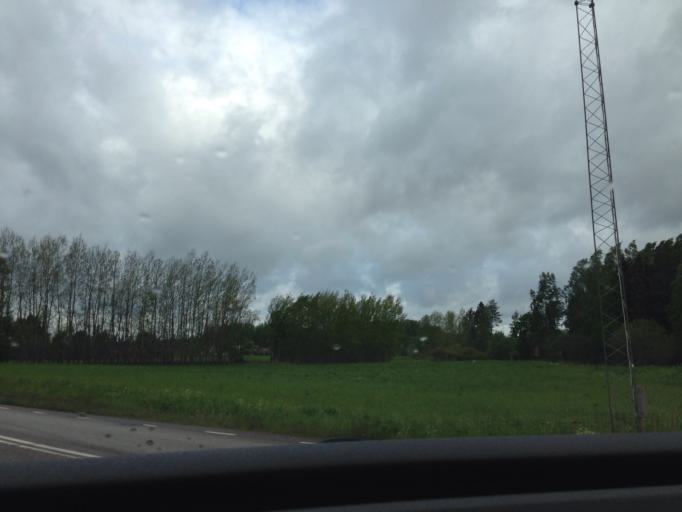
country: SE
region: Vaestra Goetaland
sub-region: Tibro Kommun
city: Tibro
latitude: 58.4205
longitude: 14.1295
